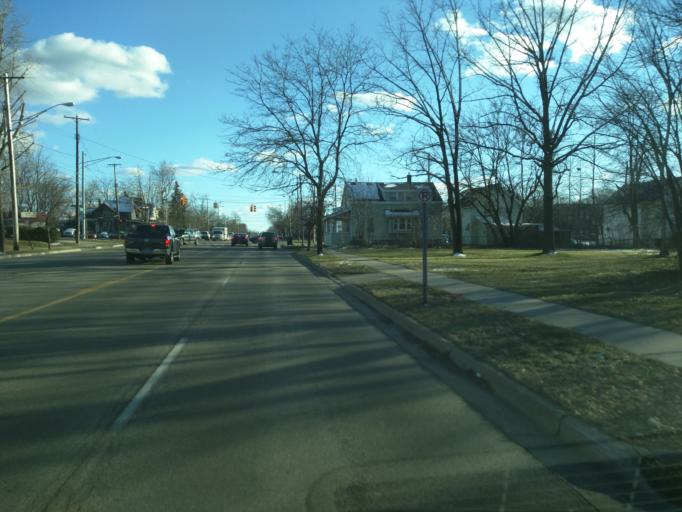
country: US
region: Michigan
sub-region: Ingham County
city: Lansing
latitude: 42.7416
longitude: -84.5379
